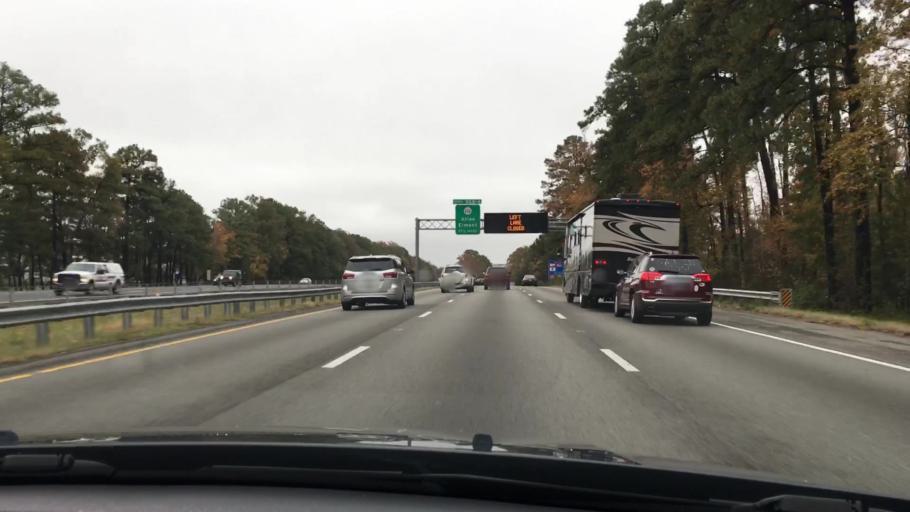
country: US
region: Virginia
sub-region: Hanover County
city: Ashland
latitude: 37.7109
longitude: -77.4482
